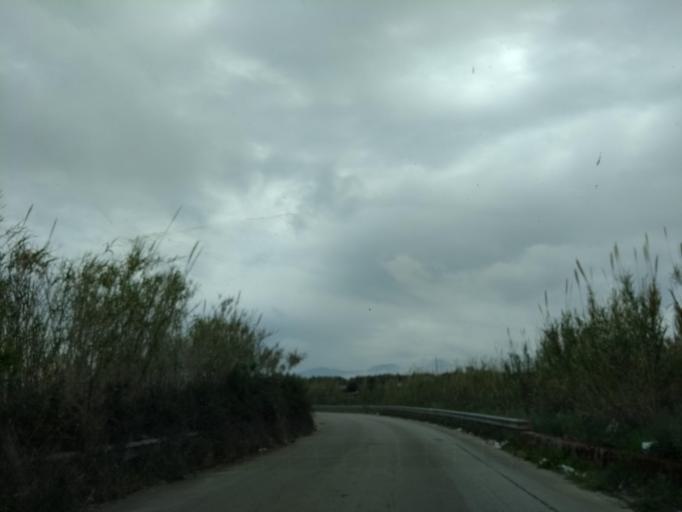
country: IT
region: Sicily
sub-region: Palermo
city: Partinico
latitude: 38.0099
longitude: 13.0663
